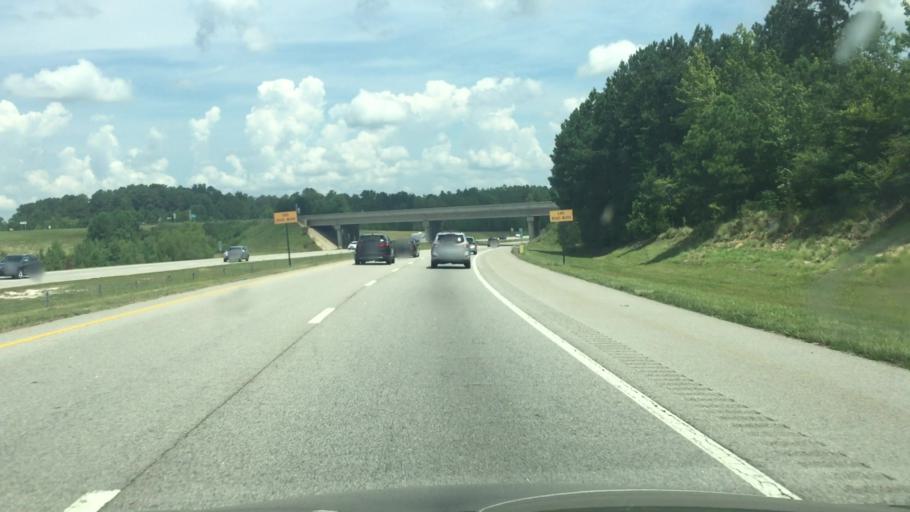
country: US
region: North Carolina
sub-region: Richmond County
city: Ellerbe
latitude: 35.0416
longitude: -79.7680
